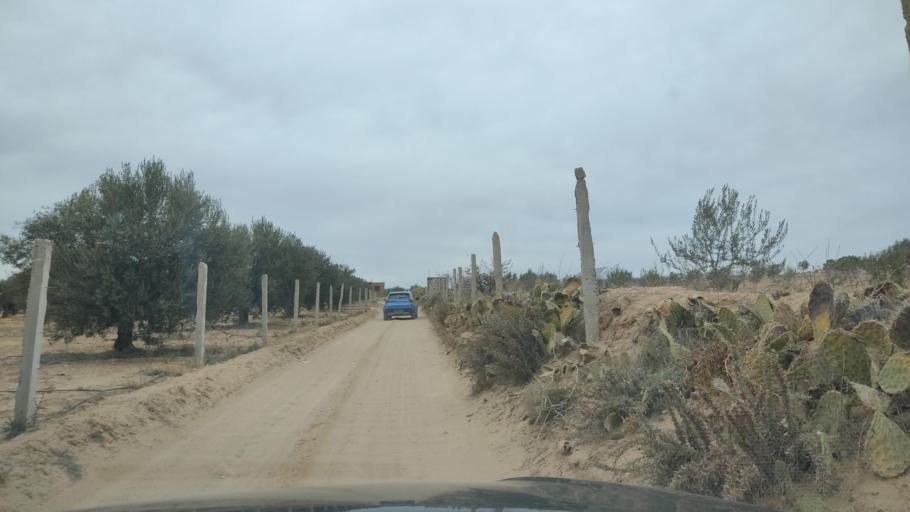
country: TN
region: Al Qasrayn
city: Kasserine
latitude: 35.2282
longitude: 8.9142
